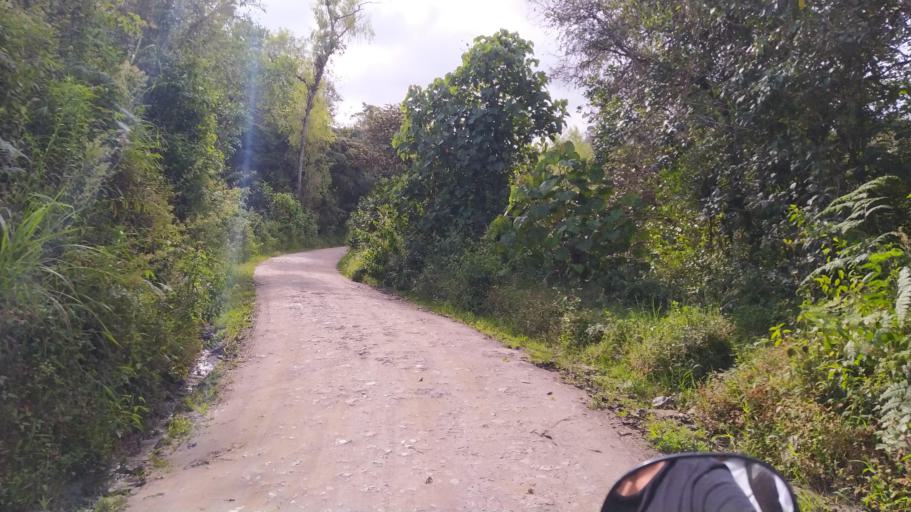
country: CO
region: Cundinamarca
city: Tenza
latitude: 5.0922
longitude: -73.4580
